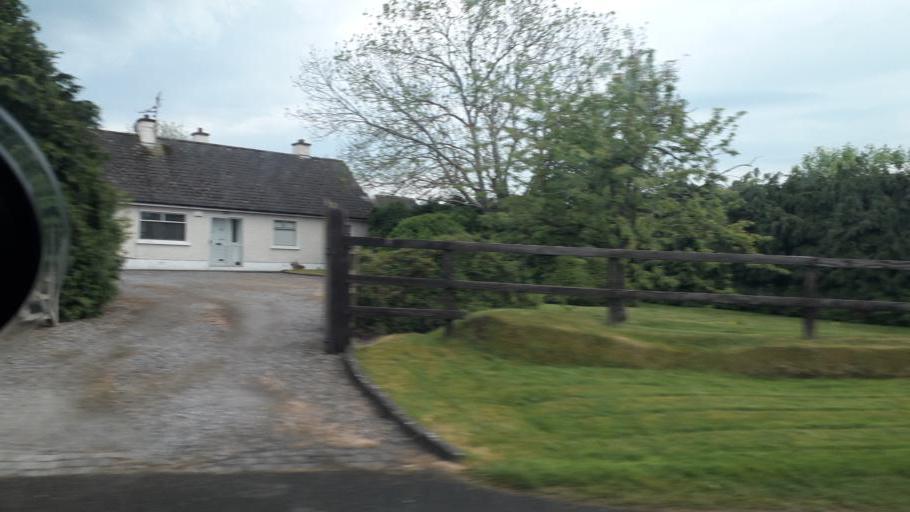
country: IE
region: Leinster
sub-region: Kildare
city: Celbridge
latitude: 53.2980
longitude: -6.5678
